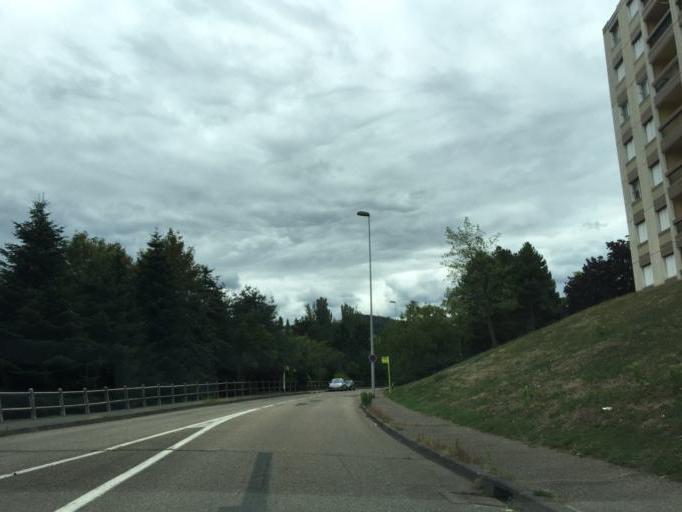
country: FR
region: Rhone-Alpes
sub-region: Departement de la Loire
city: Saint-Chamond
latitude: 45.4760
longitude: 4.5364
